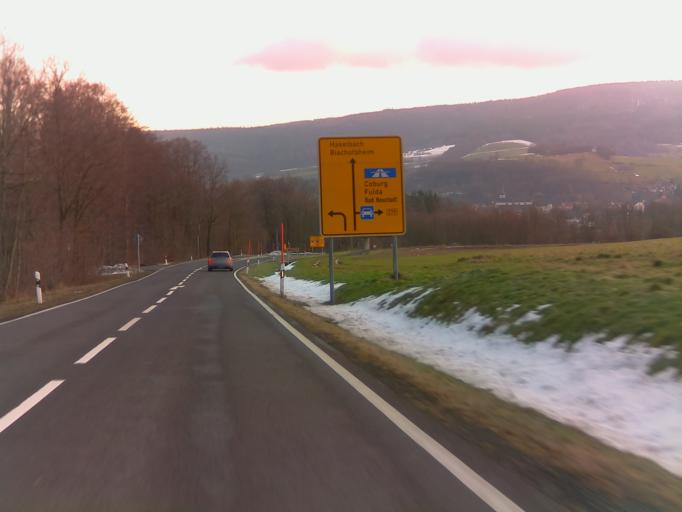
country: DE
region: Bavaria
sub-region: Regierungsbezirk Unterfranken
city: Bischofsheim an der Rhon
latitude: 50.4140
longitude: 10.0013
